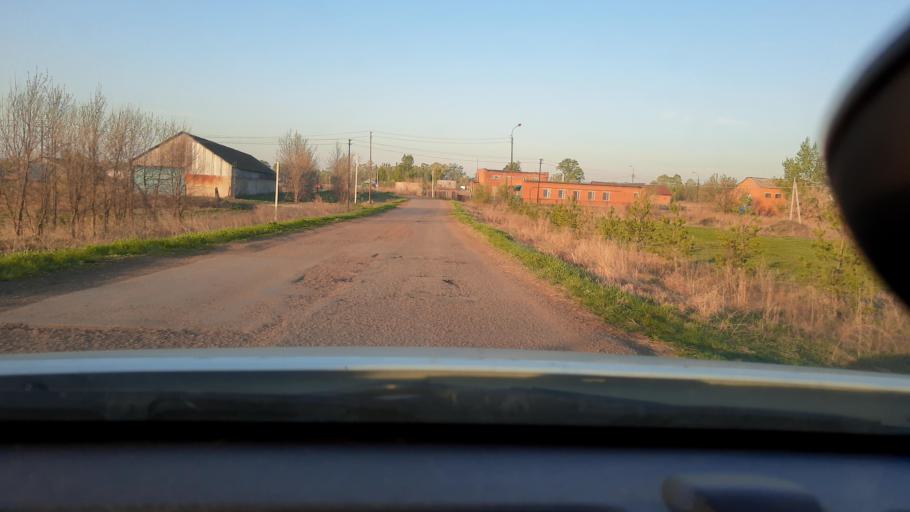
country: RU
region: Bashkortostan
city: Avdon
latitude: 54.5095
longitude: 55.8176
